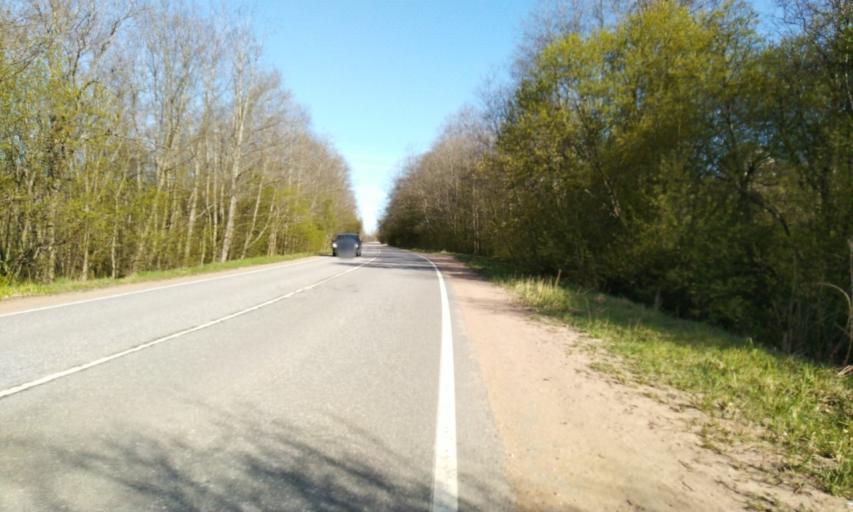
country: RU
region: Leningrad
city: Leskolovo
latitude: 60.3251
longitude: 30.4276
